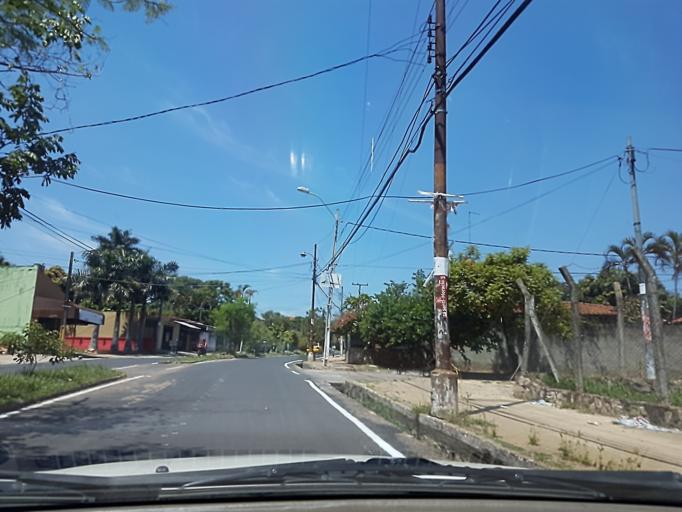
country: PY
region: Central
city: Fernando de la Mora
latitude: -25.2843
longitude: -57.5238
